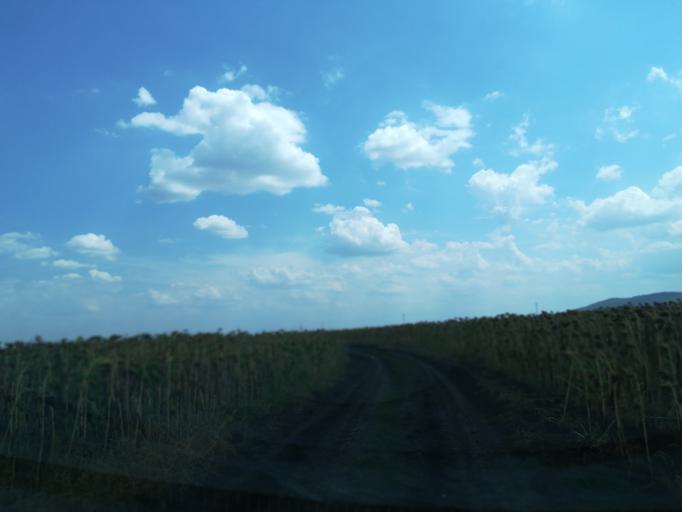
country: BG
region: Khaskovo
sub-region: Obshtina Mineralni Bani
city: Mineralni Bani
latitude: 42.0048
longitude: 25.2083
